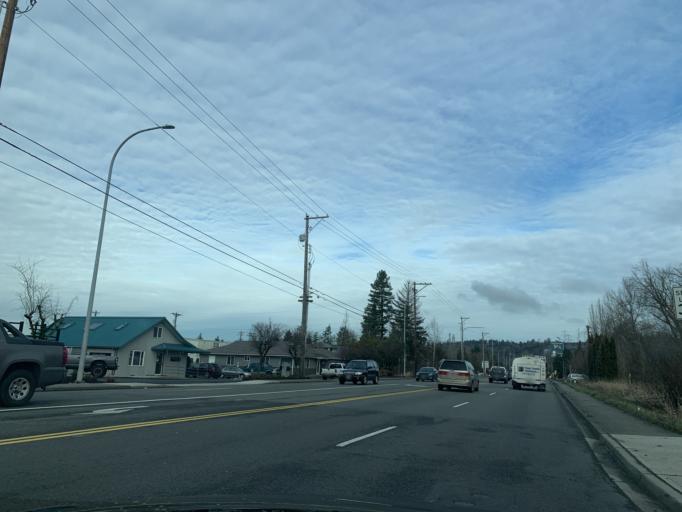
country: US
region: Washington
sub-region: Pierce County
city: Fife
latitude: 47.2502
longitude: -122.3568
